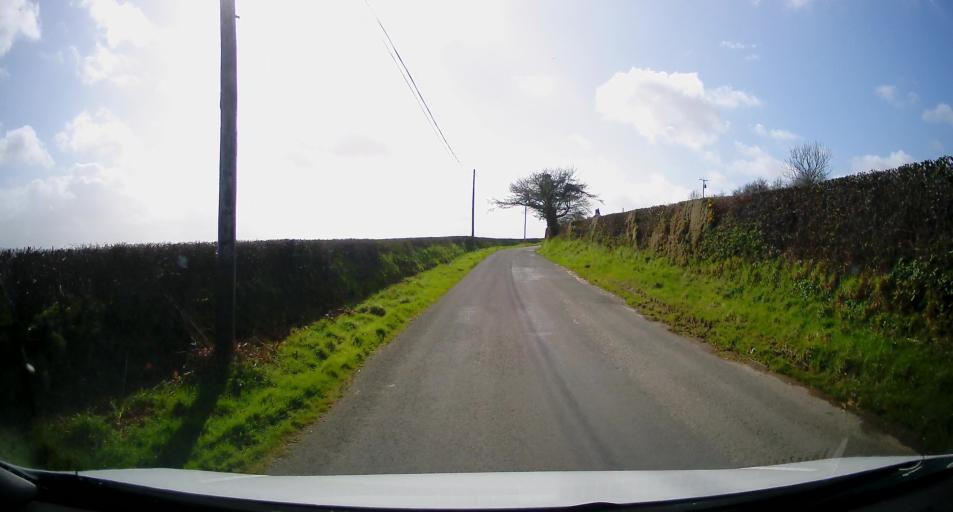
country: GB
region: Wales
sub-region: County of Ceredigion
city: Aberporth
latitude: 52.0793
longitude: -4.5442
